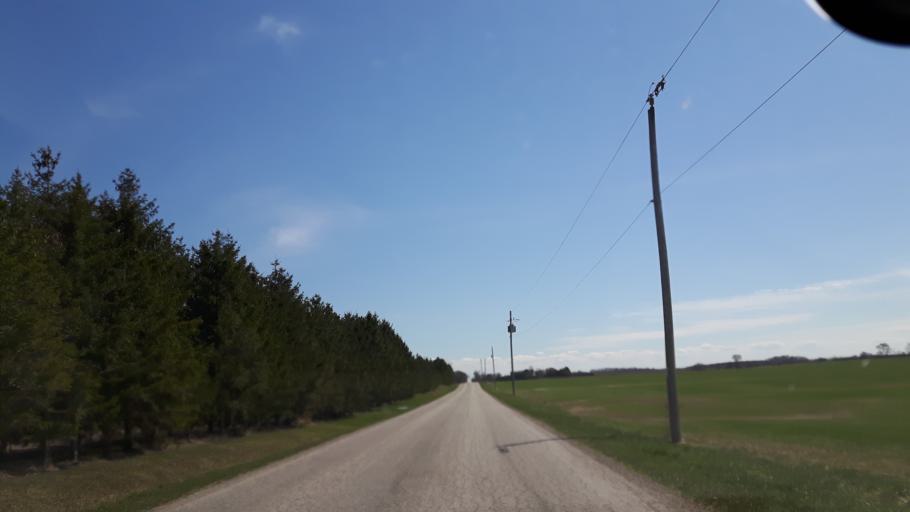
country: CA
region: Ontario
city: Goderich
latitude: 43.6421
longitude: -81.6440
